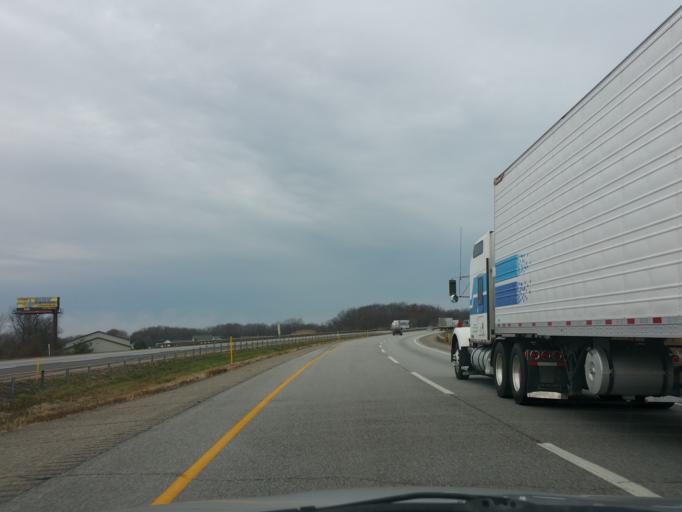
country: US
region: Indiana
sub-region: Porter County
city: Portage
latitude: 41.5725
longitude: -87.1498
